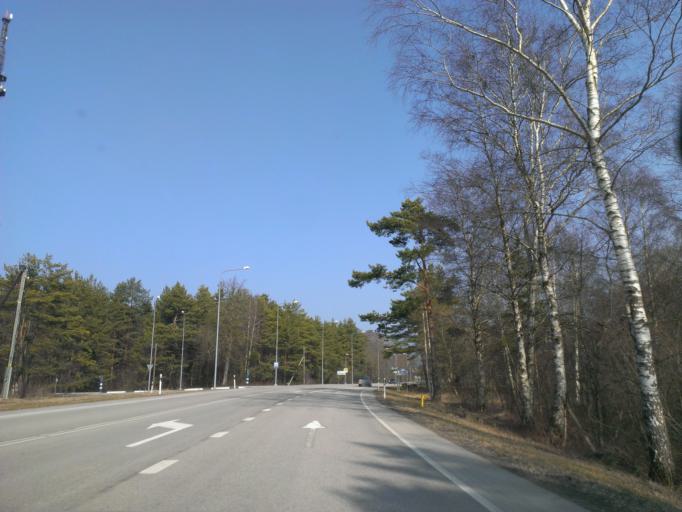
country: EE
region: Saare
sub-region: Orissaare vald
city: Orissaare
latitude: 58.5557
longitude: 23.0662
